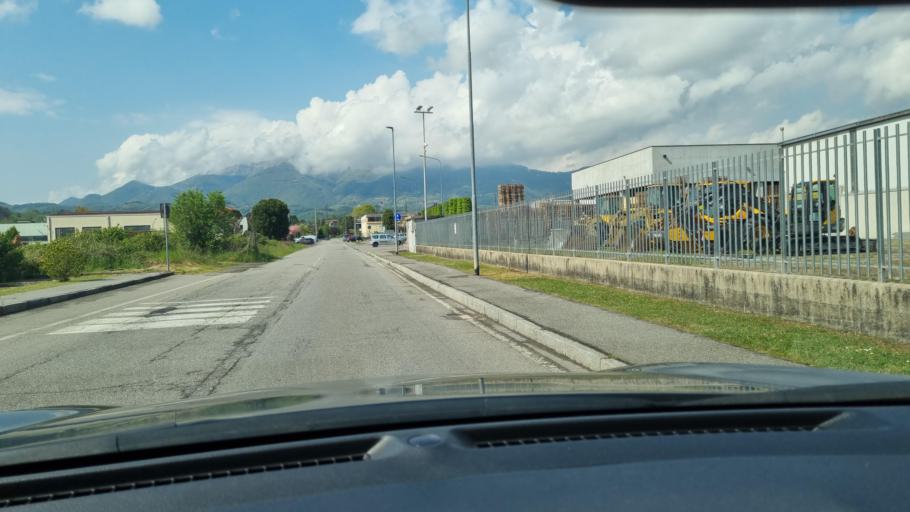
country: IT
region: Lombardy
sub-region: Provincia di Bergamo
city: Mapello
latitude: 45.7037
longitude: 9.5562
